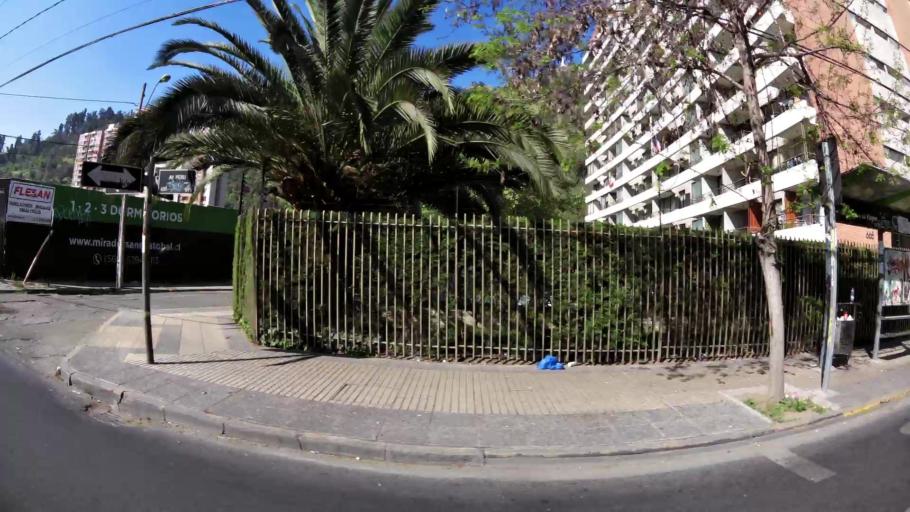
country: CL
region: Santiago Metropolitan
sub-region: Provincia de Santiago
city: Santiago
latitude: -33.4250
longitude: -70.6397
